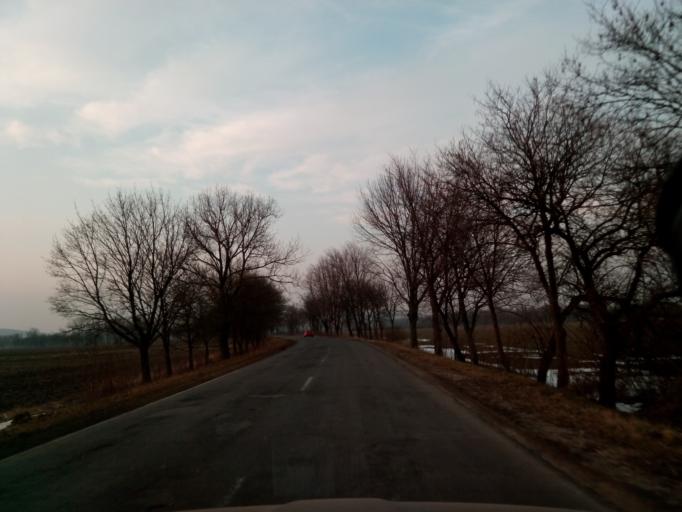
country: HU
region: Borsod-Abauj-Zemplen
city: Gonc
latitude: 48.4890
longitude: 21.2514
